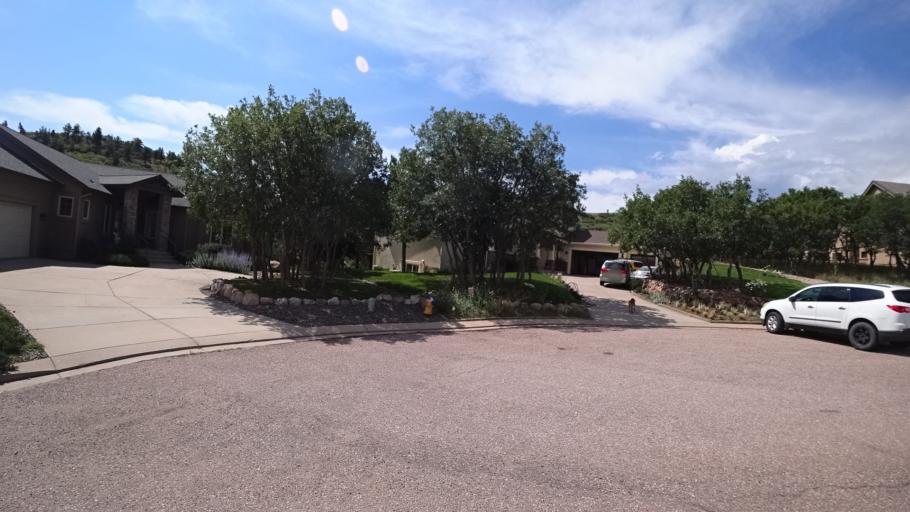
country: US
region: Colorado
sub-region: El Paso County
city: Air Force Academy
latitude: 38.9456
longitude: -104.8780
